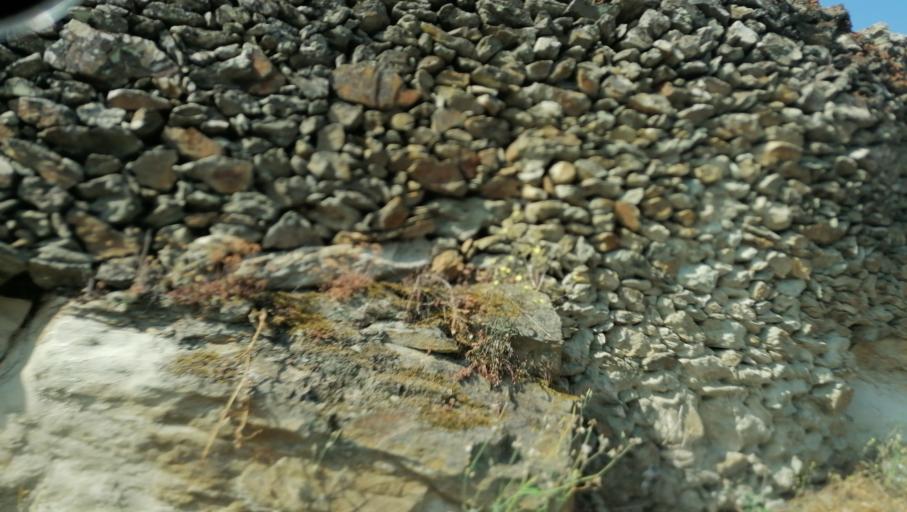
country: PT
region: Vila Real
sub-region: Sabrosa
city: Vilela
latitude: 41.2013
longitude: -7.5474
